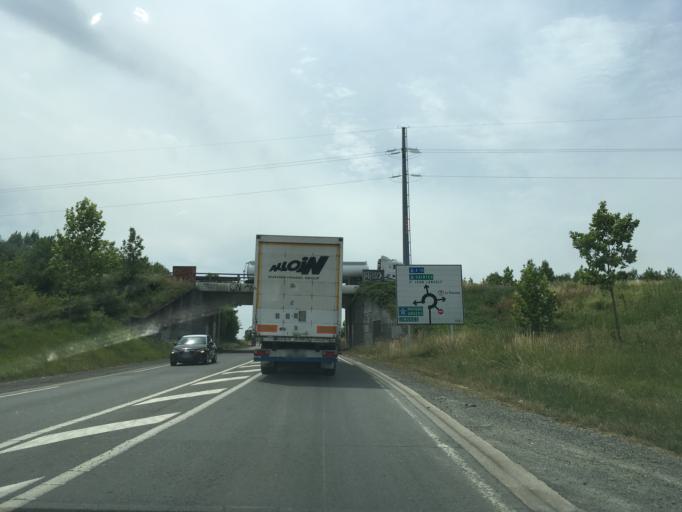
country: FR
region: Poitou-Charentes
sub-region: Departement des Deux-Sevres
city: Niort
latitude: 46.2955
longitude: -0.4661
